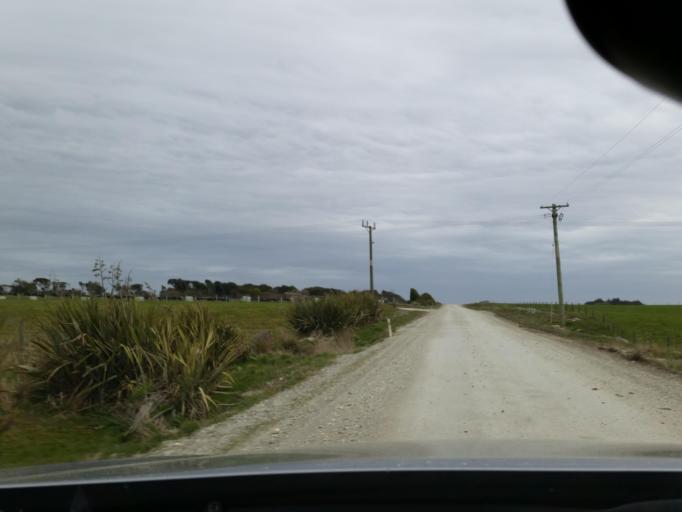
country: NZ
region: Southland
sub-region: Invercargill City
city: Invercargill
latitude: -46.4335
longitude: 168.5062
